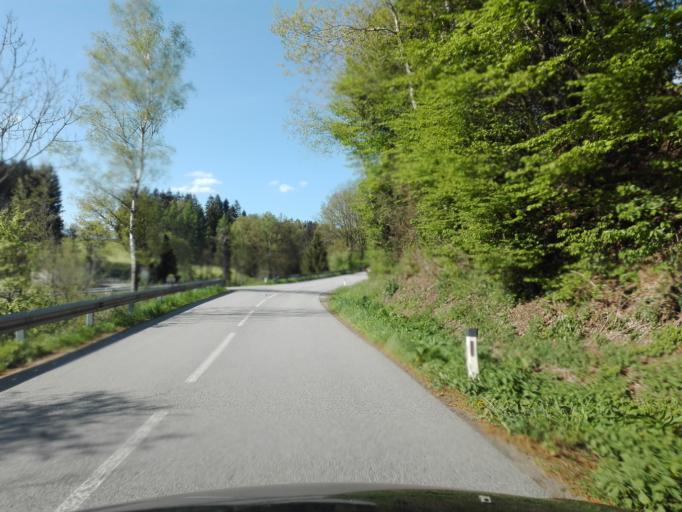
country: DE
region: Bavaria
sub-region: Lower Bavaria
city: Obernzell
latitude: 48.4896
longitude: 13.5770
